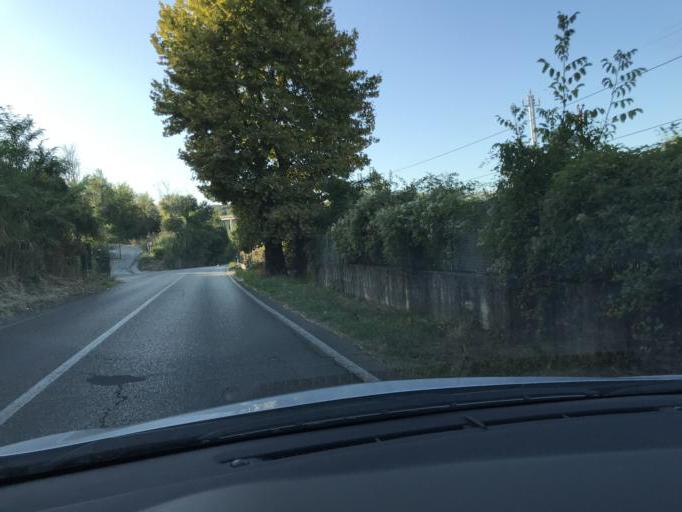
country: IT
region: Latium
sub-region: Provincia di Viterbo
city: Orte
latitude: 42.4478
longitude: 12.3922
